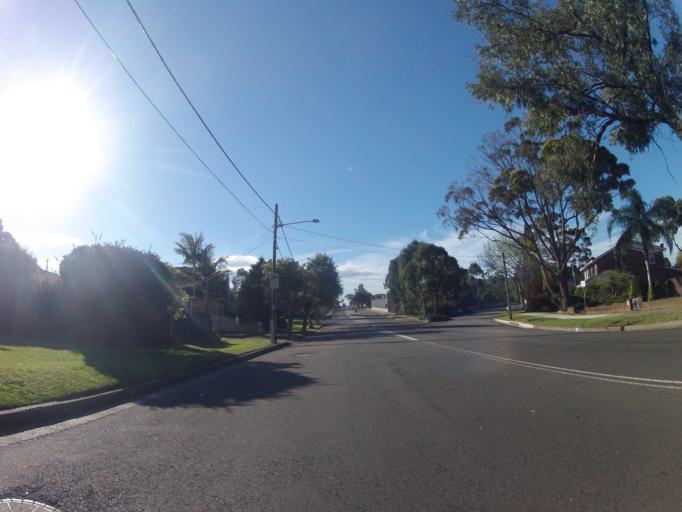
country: AU
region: New South Wales
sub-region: Canterbury
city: Roselands
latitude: -33.9435
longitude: 151.0803
